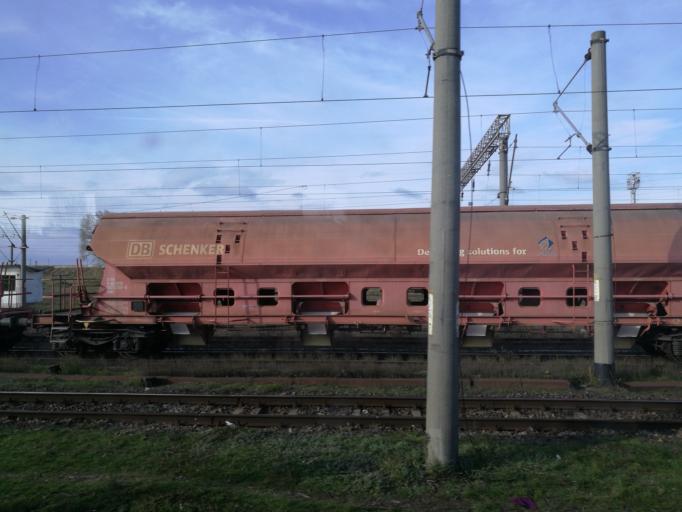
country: RO
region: Vrancea
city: Marasheshty
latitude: 45.8732
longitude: 27.2142
